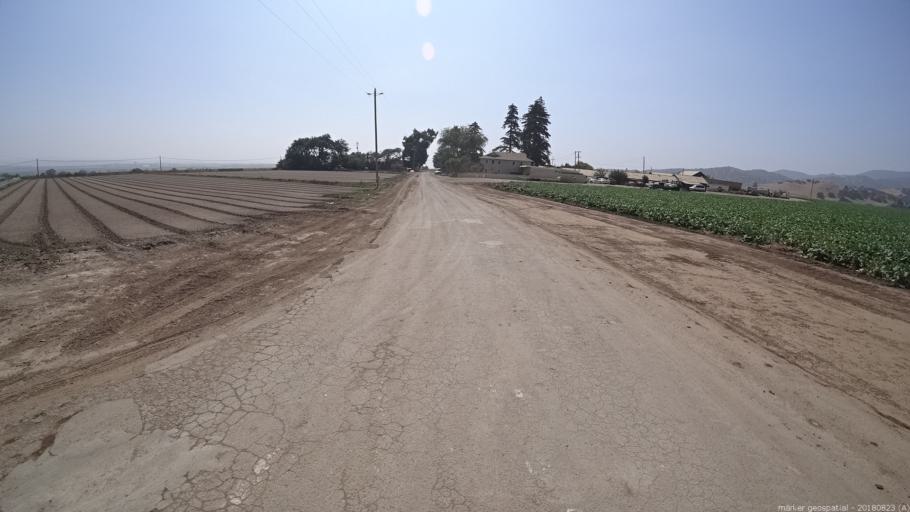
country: US
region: California
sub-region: Monterey County
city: King City
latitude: 36.2334
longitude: -121.1768
